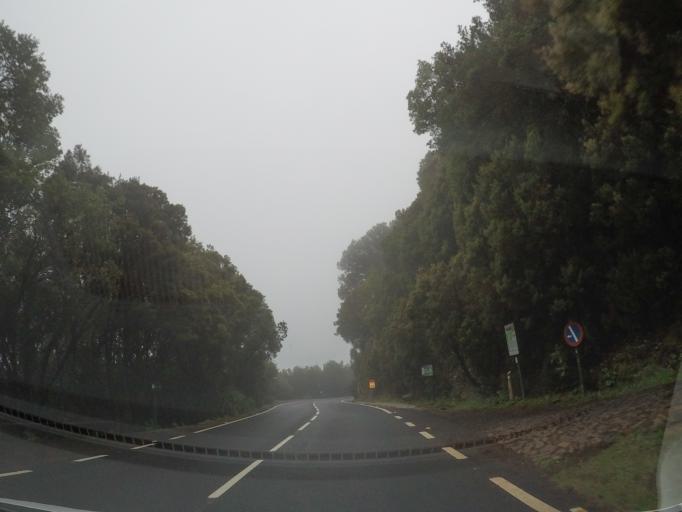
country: ES
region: Canary Islands
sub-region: Provincia de Santa Cruz de Tenerife
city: Alajero
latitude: 28.1155
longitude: -17.2432
